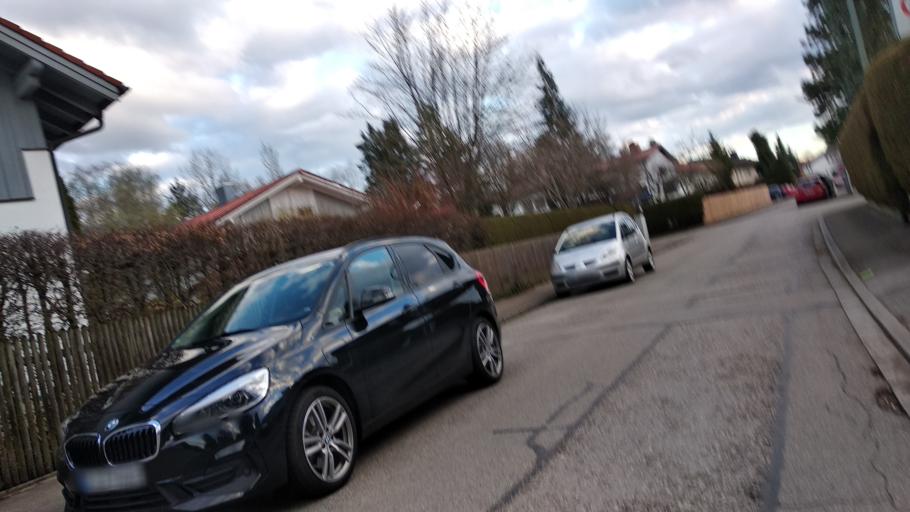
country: DE
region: Bavaria
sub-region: Upper Bavaria
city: Ottobrunn
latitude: 48.0775
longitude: 11.6843
